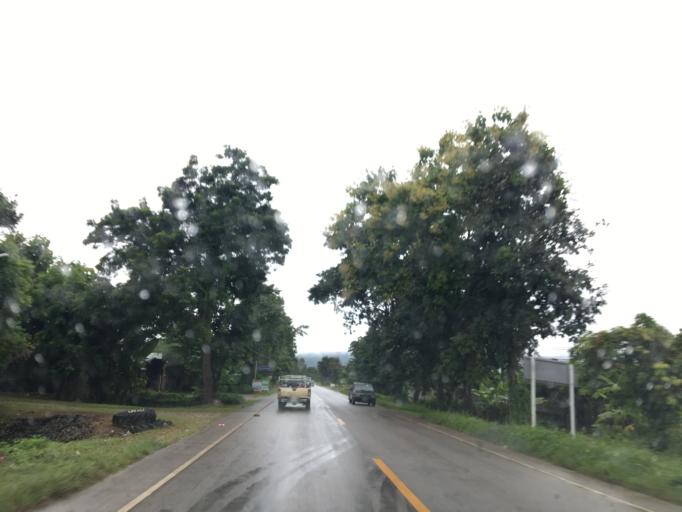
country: TH
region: Chiang Rai
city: Pa Daet
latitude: 19.4992
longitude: 99.9868
